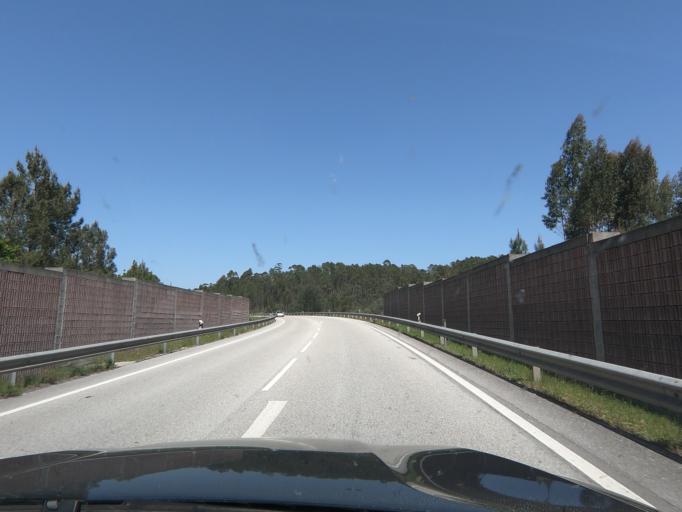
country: PT
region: Coimbra
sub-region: Miranda do Corvo
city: Miranda do Corvo
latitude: 40.1063
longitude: -8.2973
